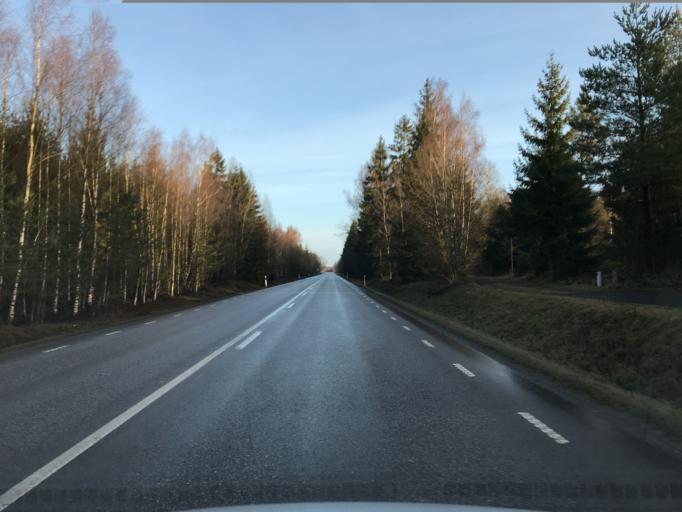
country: SE
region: Skane
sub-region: Hassleholms Kommun
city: Bjarnum
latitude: 56.2446
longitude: 13.7145
